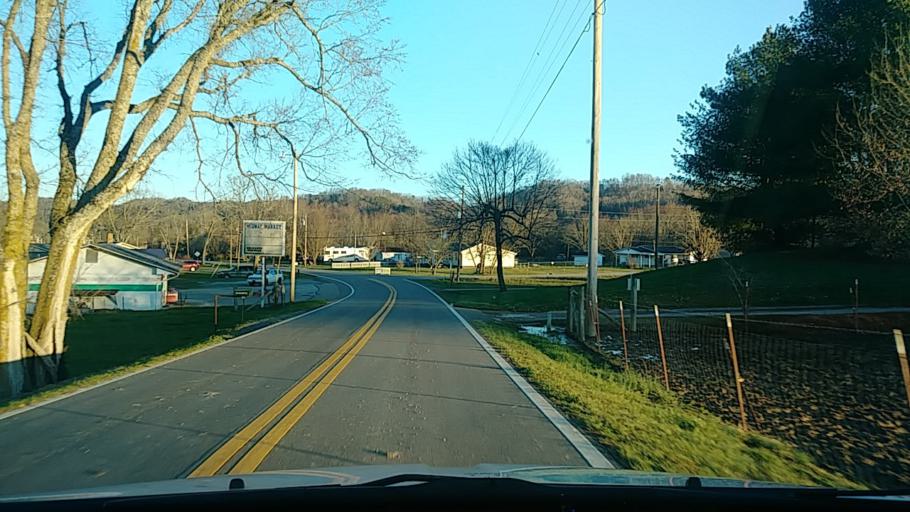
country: US
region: Tennessee
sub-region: Greene County
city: Mosheim
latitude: 36.1193
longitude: -83.0411
